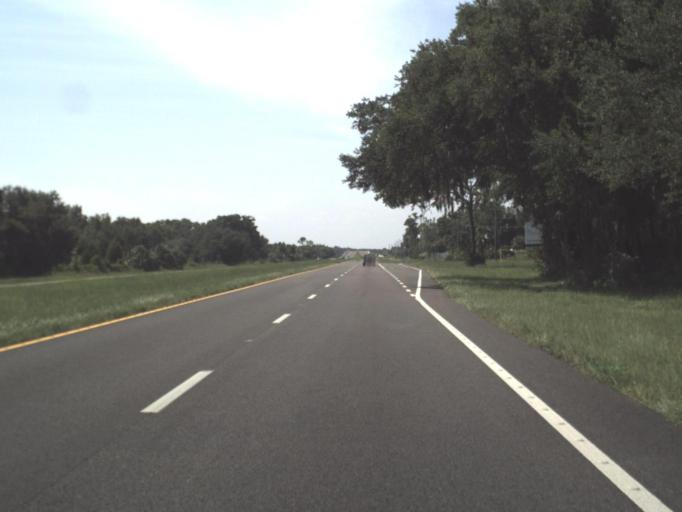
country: US
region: Florida
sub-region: Levy County
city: Inglis
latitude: 29.0016
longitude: -82.6559
